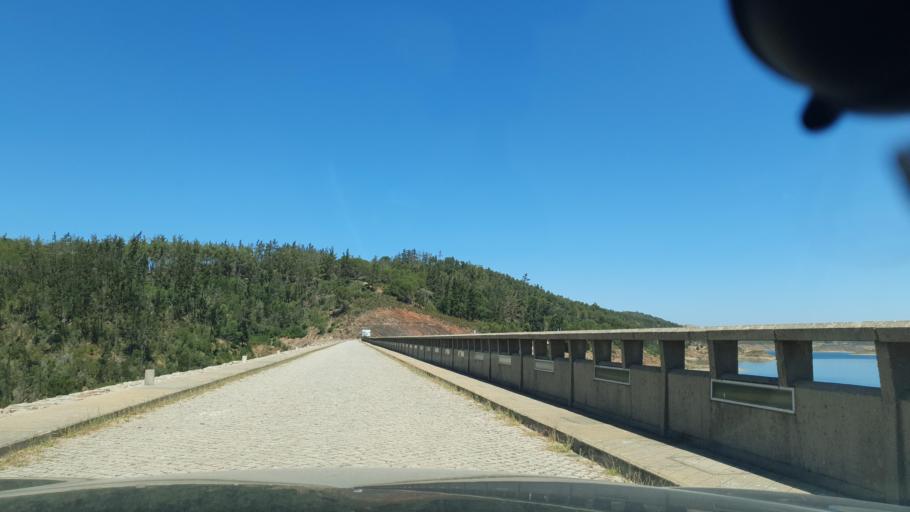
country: PT
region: Beja
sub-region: Odemira
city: Odemira
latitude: 37.5131
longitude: -8.4414
